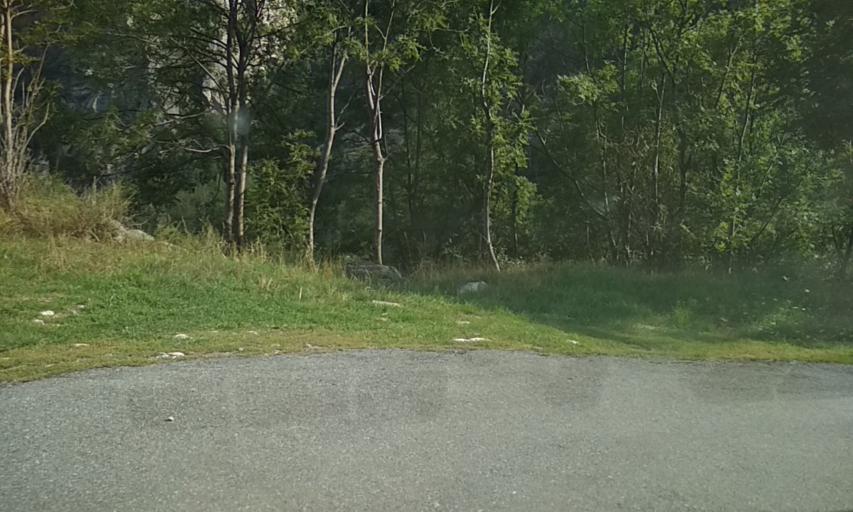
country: IT
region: Piedmont
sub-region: Provincia di Torino
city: Noasca
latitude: 45.4545
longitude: 7.3044
